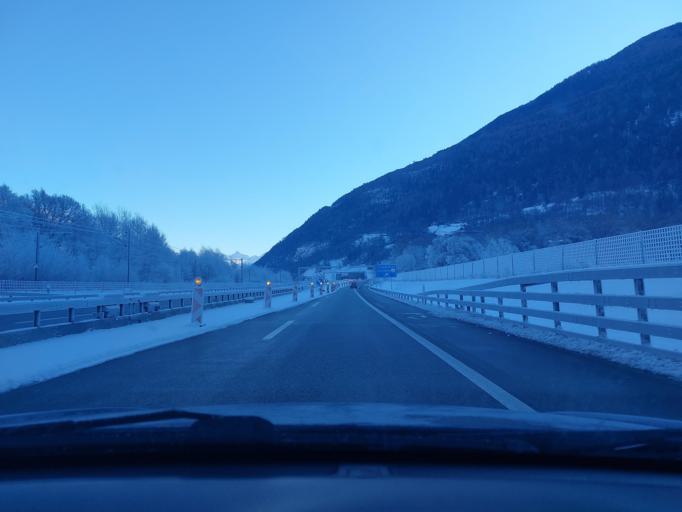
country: CH
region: Valais
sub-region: Leuk District
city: Gampel
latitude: 46.3066
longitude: 7.7313
